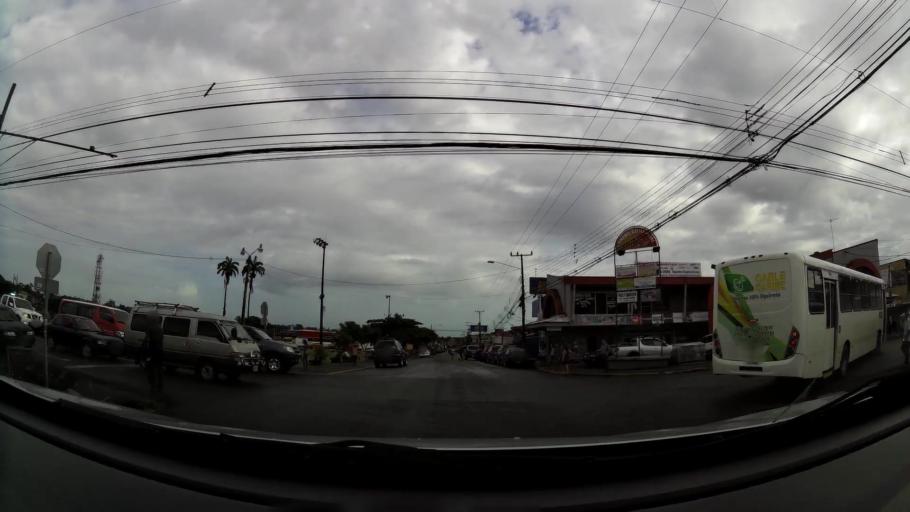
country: CR
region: Limon
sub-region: Canton de Siquirres
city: Siquirres
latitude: 10.0956
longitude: -83.5063
